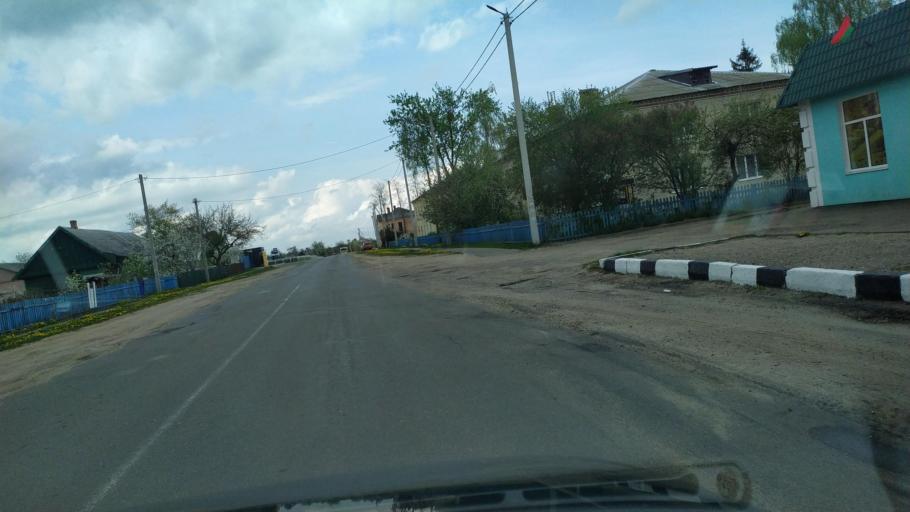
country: BY
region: Brest
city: Pruzhany
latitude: 52.5663
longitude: 24.4191
